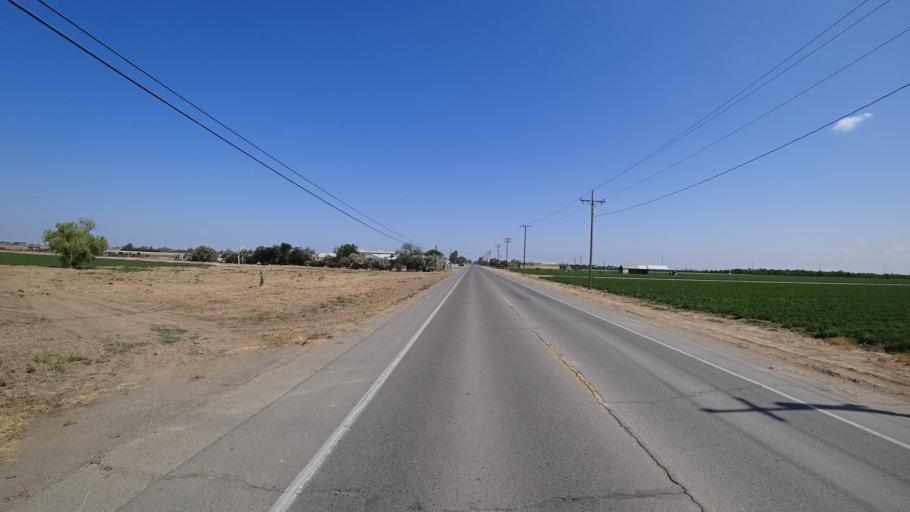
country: US
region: California
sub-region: Kings County
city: Home Garden
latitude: 36.2870
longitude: -119.6370
